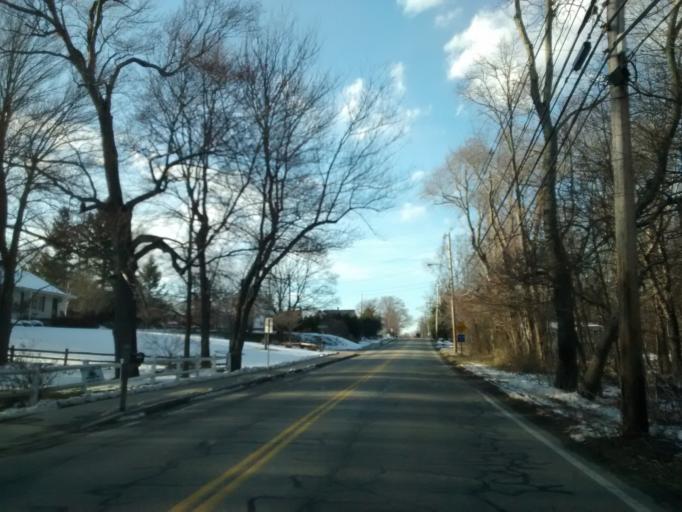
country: US
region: Massachusetts
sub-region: Middlesex County
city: Hopkinton
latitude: 42.2139
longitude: -71.5150
